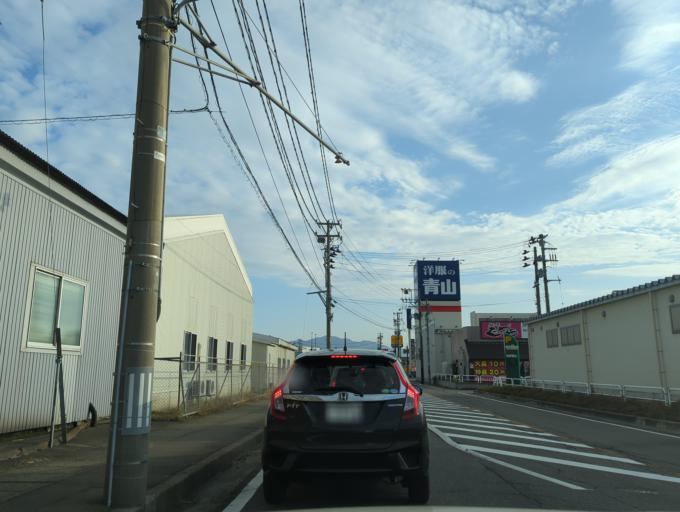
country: JP
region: Niigata
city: Kashiwazaki
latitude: 37.3623
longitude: 138.5636
